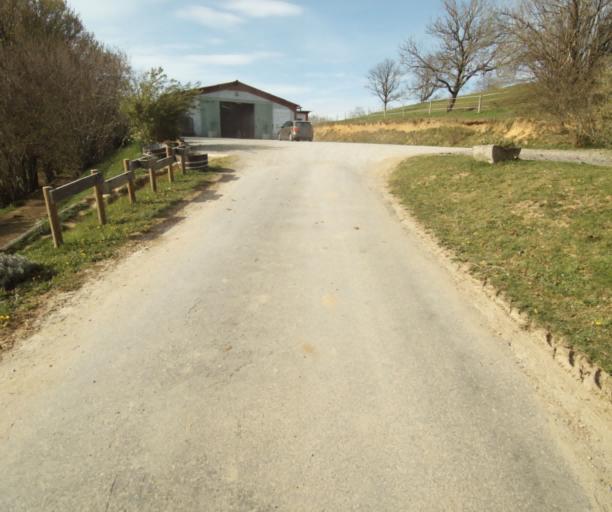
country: FR
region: Limousin
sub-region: Departement de la Correze
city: Saint-Clement
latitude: 45.3184
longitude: 1.7177
